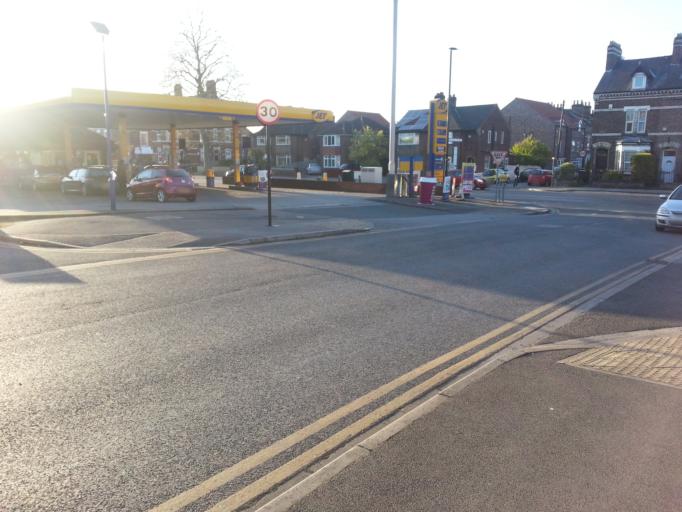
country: GB
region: England
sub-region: City of York
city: Heslington
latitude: 53.9542
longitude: -1.0634
